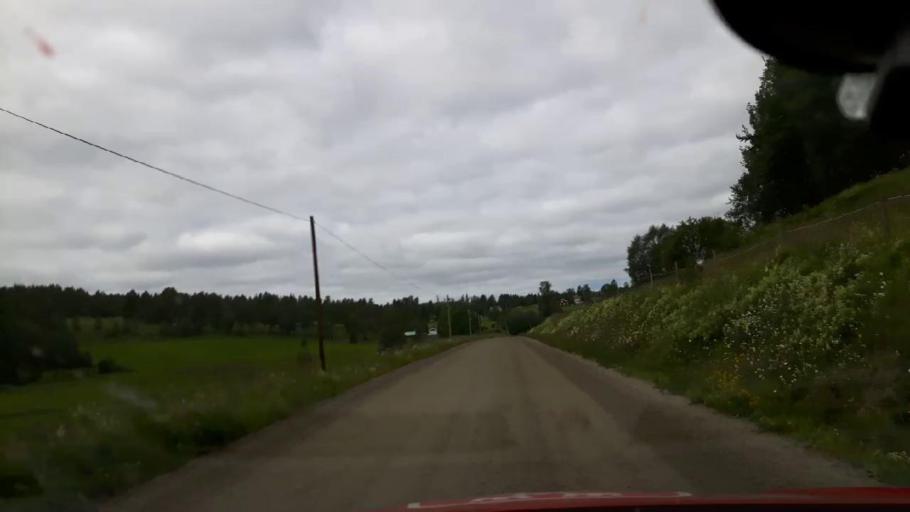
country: SE
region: Jaemtland
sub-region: OEstersunds Kommun
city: Brunflo
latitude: 62.9171
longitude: 15.0221
